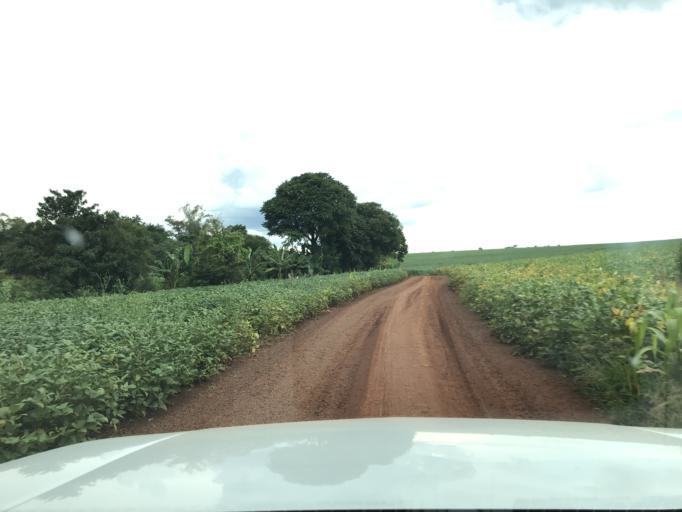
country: BR
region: Parana
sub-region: Palotina
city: Palotina
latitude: -24.2747
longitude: -53.7900
